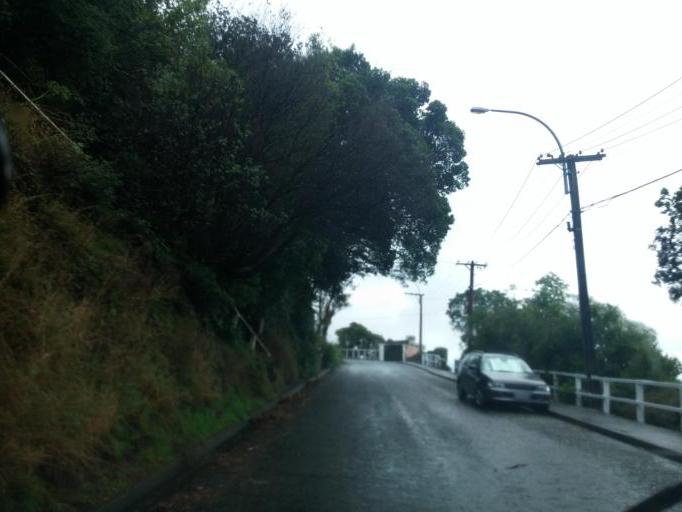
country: NZ
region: Wellington
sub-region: Wellington City
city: Wellington
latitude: -41.2611
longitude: 174.7864
